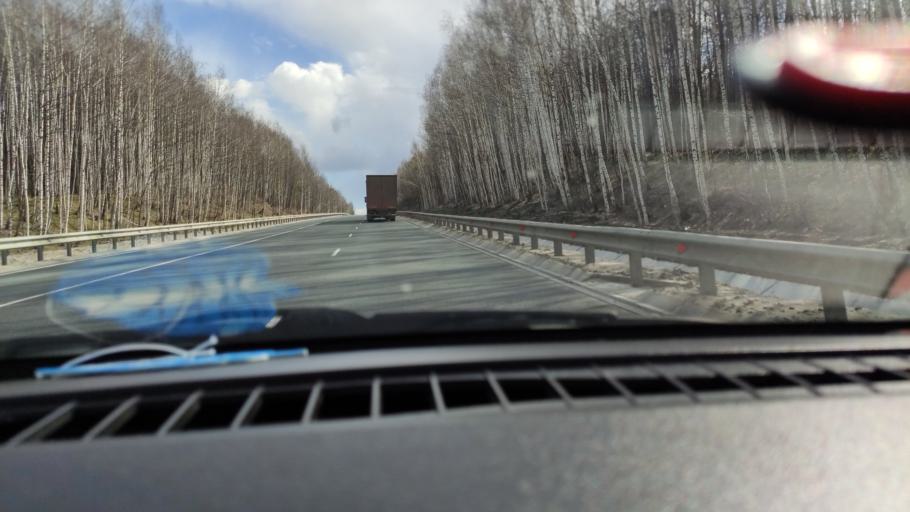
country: RU
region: Saratov
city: Khvalynsk
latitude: 52.5013
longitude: 48.0149
